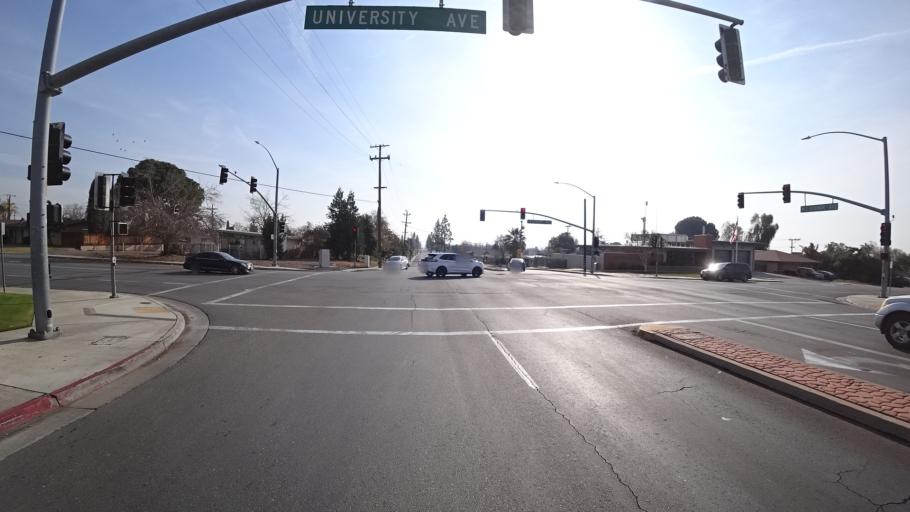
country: US
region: California
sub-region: Kern County
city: Oildale
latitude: 35.4052
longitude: -118.9676
